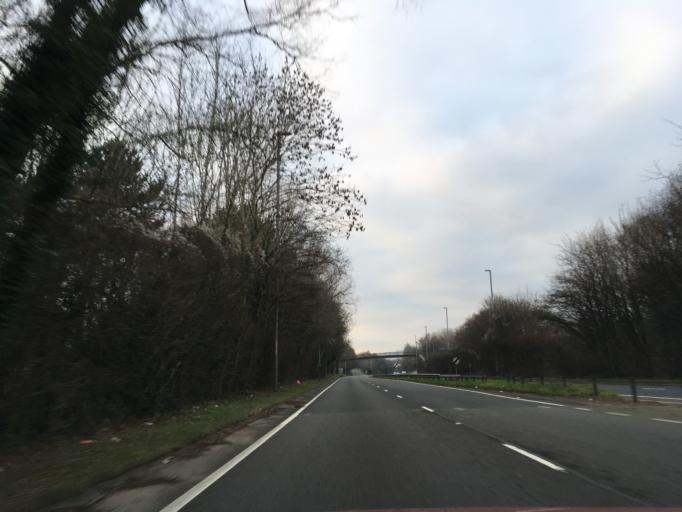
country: GB
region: Wales
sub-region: Newport
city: Newport
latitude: 51.5822
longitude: -3.0457
